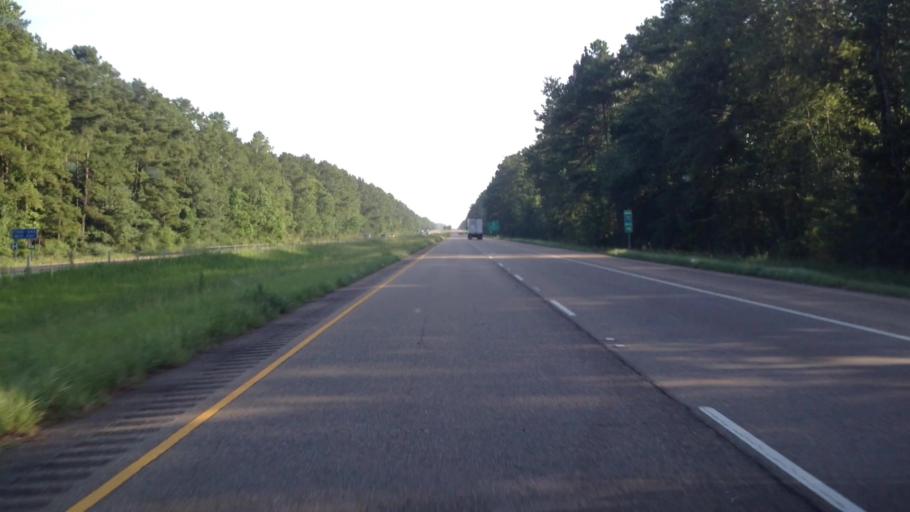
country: US
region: Louisiana
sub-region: Tangipahoa Parish
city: Amite
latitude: 30.7126
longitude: -90.5327
